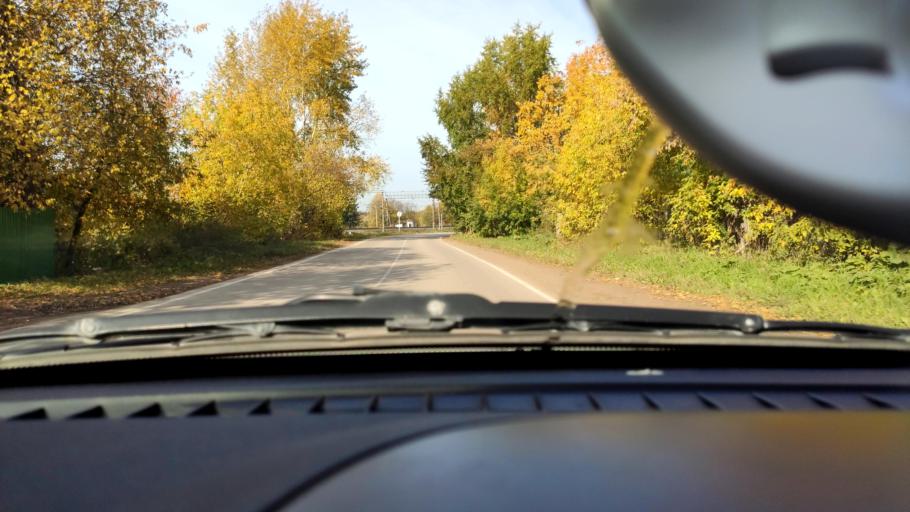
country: RU
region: Perm
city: Overyata
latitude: 58.0899
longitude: 55.8658
